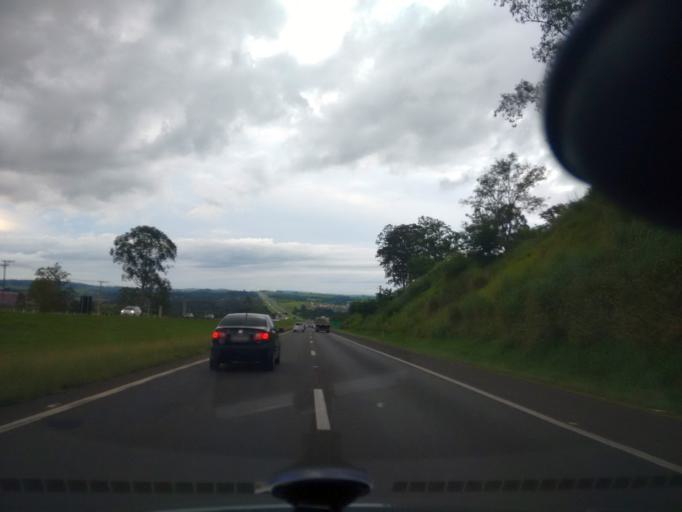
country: BR
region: Sao Paulo
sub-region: Rio Claro
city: Rio Claro
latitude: -22.4012
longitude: -47.5922
